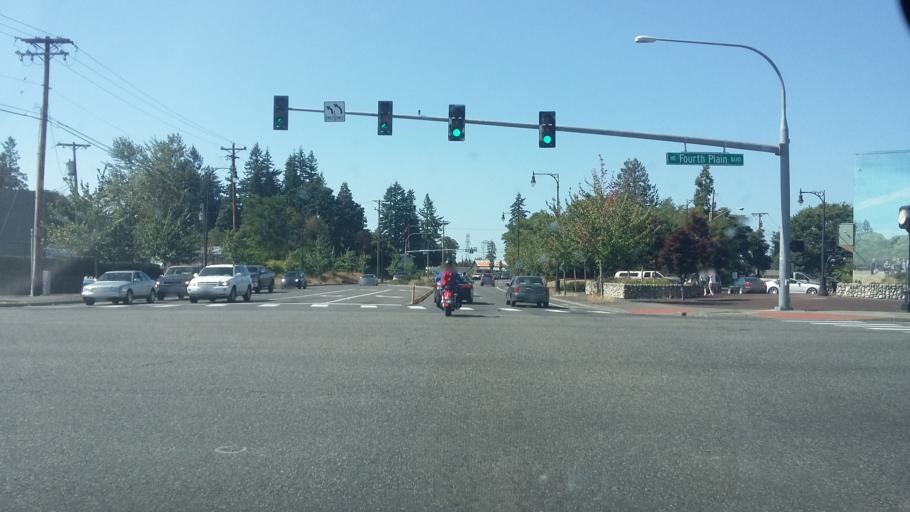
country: US
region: Washington
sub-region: Clark County
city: Orchards
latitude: 45.6648
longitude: -122.5612
